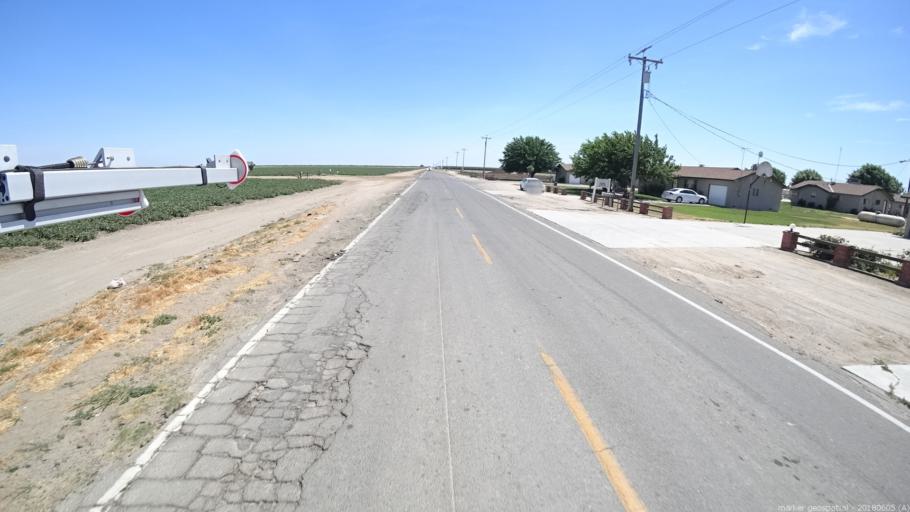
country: US
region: California
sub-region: Fresno County
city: Firebaugh
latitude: 36.9893
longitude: -120.3831
